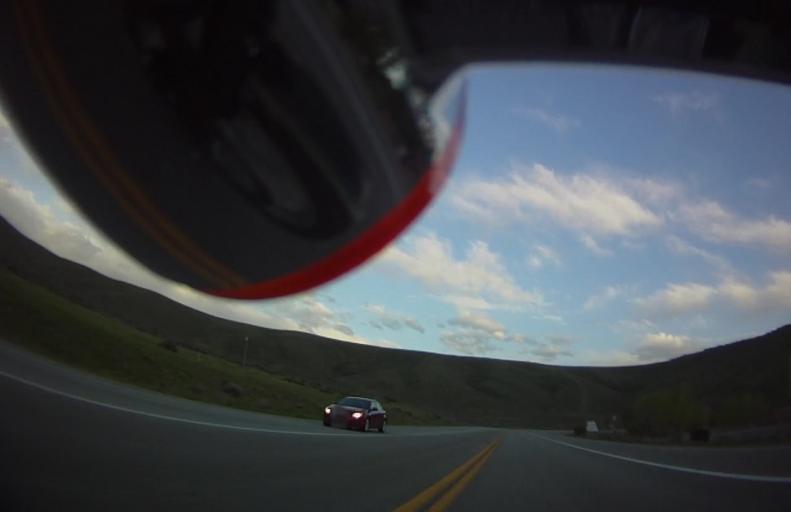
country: US
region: Utah
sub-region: Wasatch County
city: Midway
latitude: 40.4478
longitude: -111.4776
